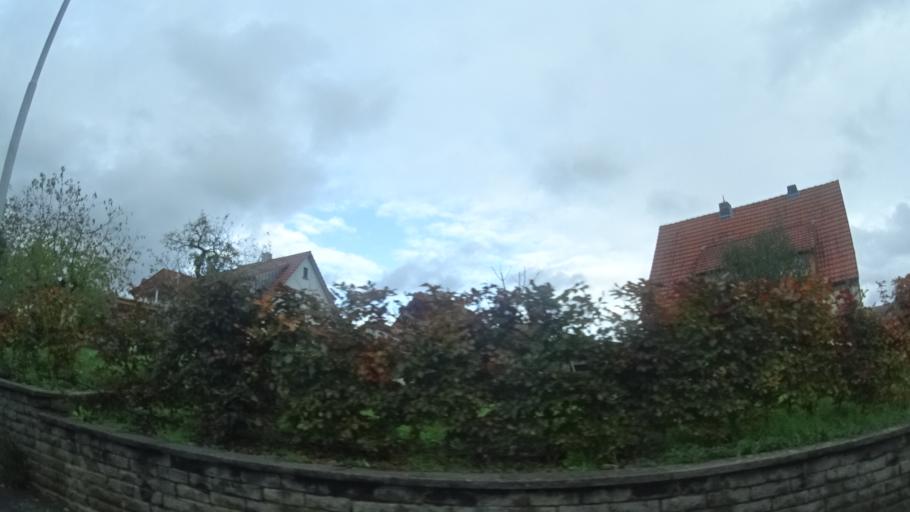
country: DE
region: Bavaria
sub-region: Regierungsbezirk Unterfranken
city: Bad Neustadt an der Saale
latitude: 50.3291
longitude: 10.2075
